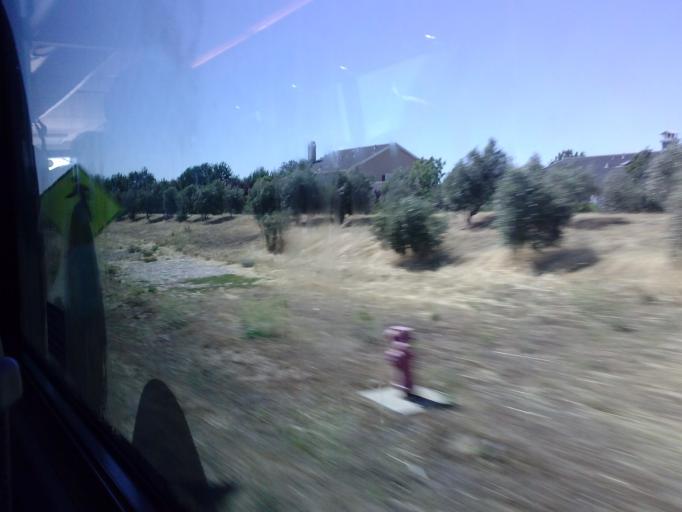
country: US
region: California
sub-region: Alameda County
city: Livermore
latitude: 37.6625
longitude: -121.7537
